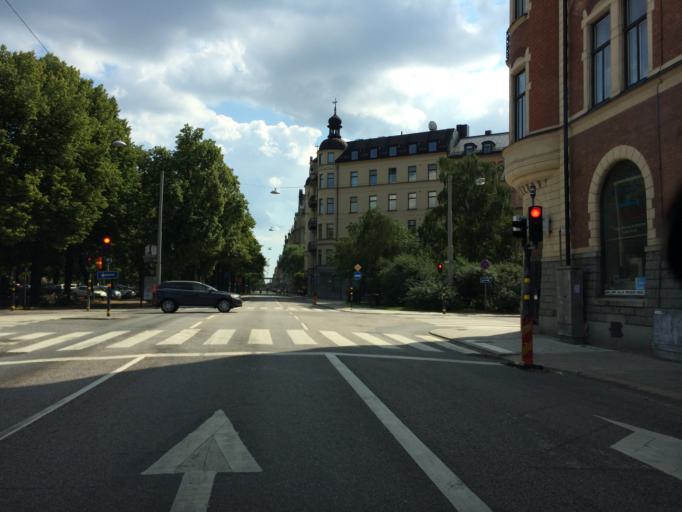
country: SE
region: Stockholm
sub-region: Stockholms Kommun
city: OEstermalm
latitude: 59.3450
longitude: 18.0728
